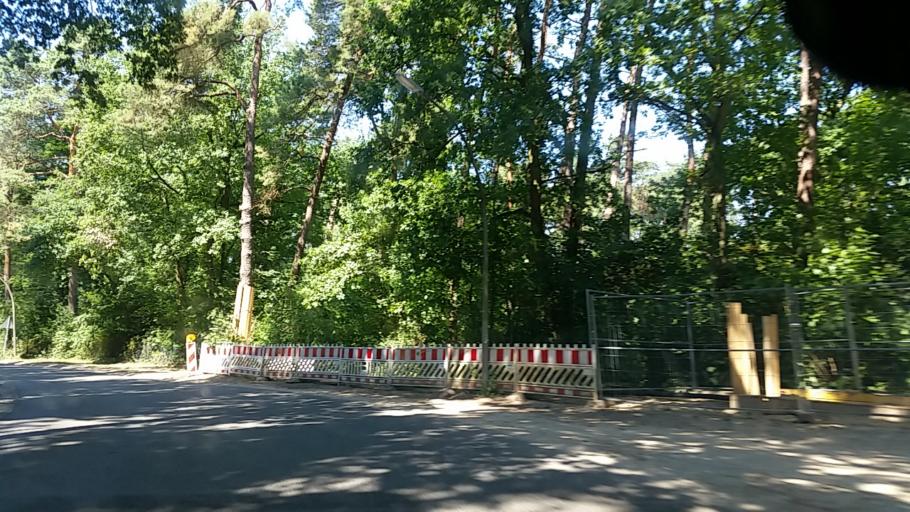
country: DE
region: Schleswig-Holstein
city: Wedel
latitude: 53.5704
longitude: 9.7635
